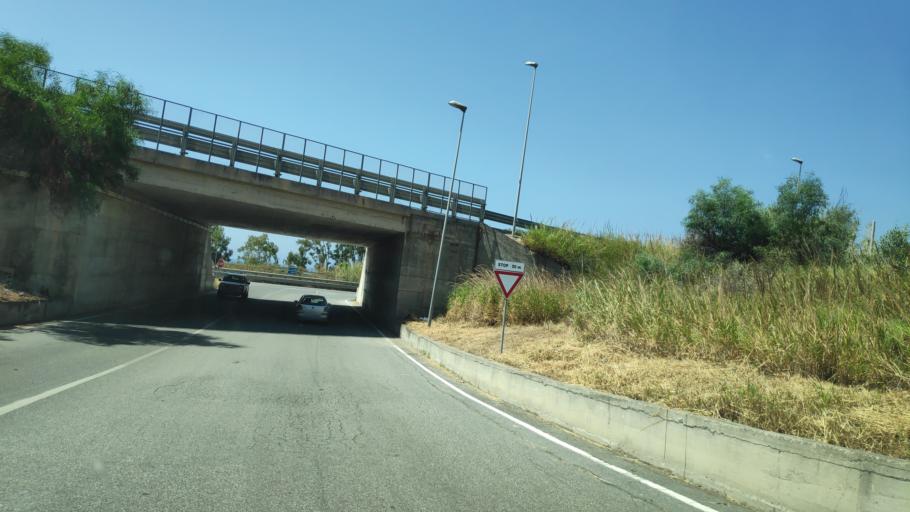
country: IT
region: Calabria
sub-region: Provincia di Reggio Calabria
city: Palizzi Marina
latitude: 37.9212
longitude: 15.9602
